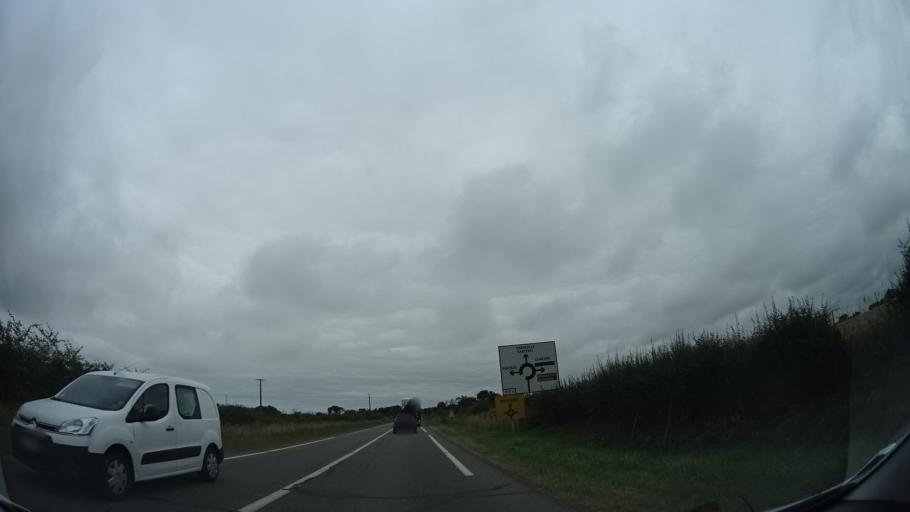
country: FR
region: Lower Normandy
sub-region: Departement de la Manche
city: Portbail
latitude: 49.3610
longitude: -1.6932
